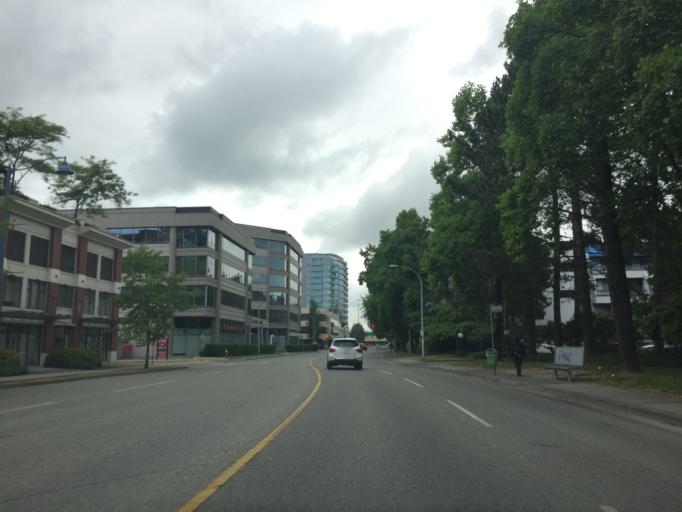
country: CA
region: British Columbia
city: Richmond
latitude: 49.1705
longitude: -123.1314
